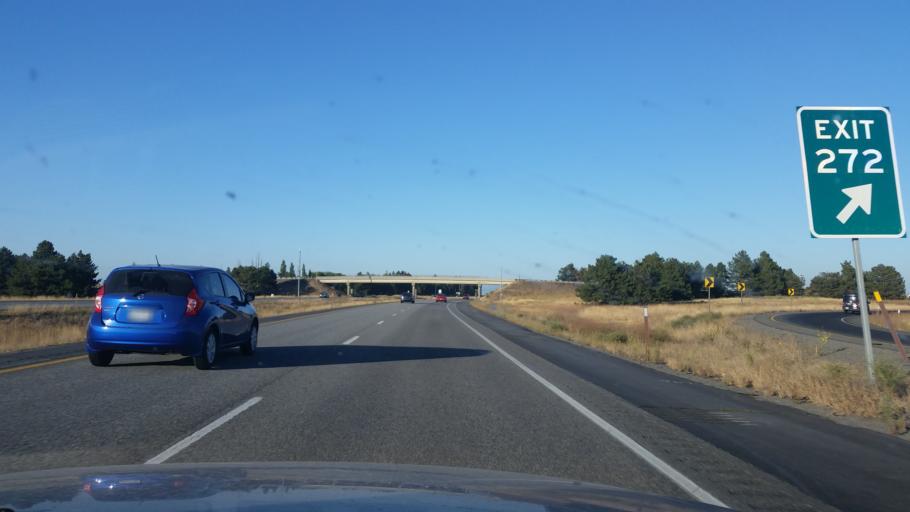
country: US
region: Washington
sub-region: Spokane County
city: Airway Heights
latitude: 47.5901
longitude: -117.5672
